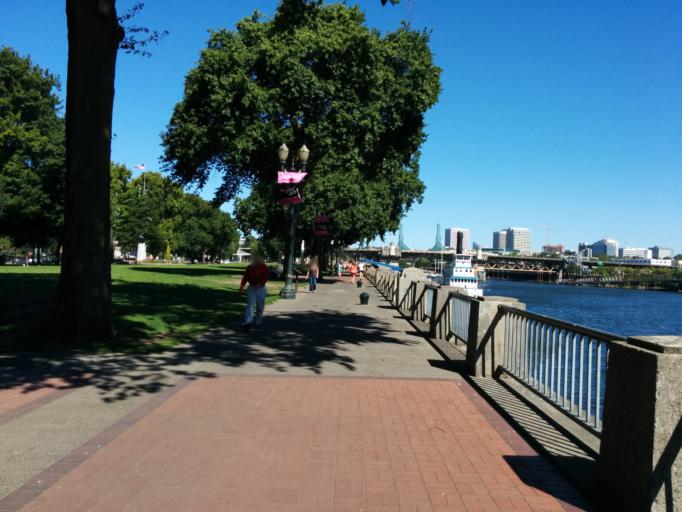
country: US
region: Oregon
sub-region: Multnomah County
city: Portland
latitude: 45.5190
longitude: -122.6708
